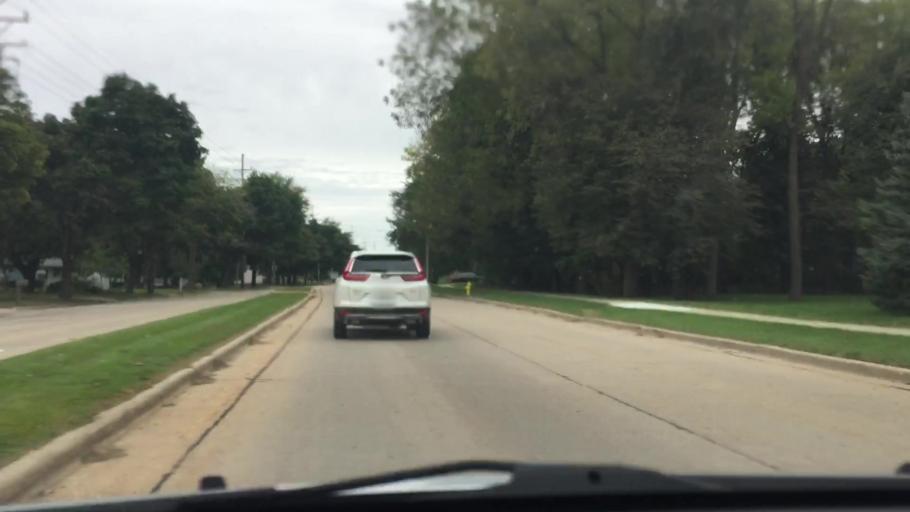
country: US
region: Wisconsin
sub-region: Waukesha County
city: Waukesha
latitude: 43.0255
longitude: -88.2417
